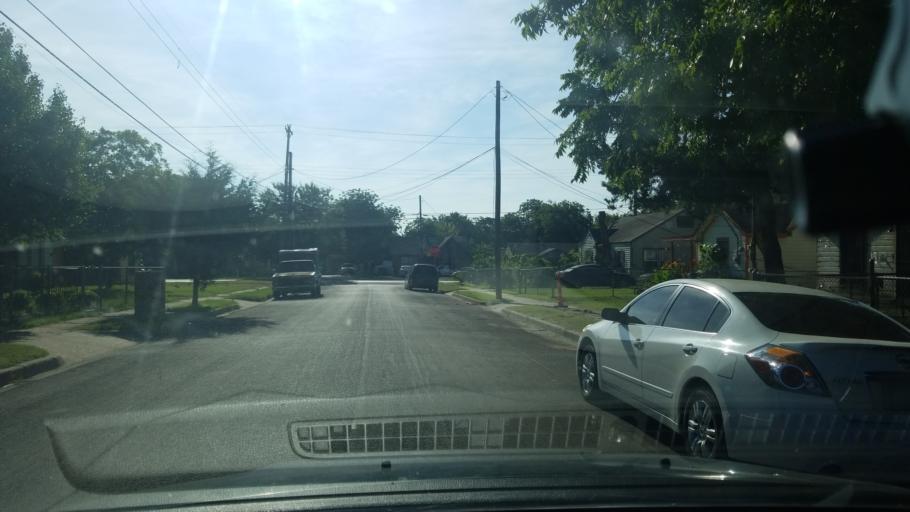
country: US
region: Texas
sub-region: Dallas County
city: Dallas
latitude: 32.7304
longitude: -96.8123
